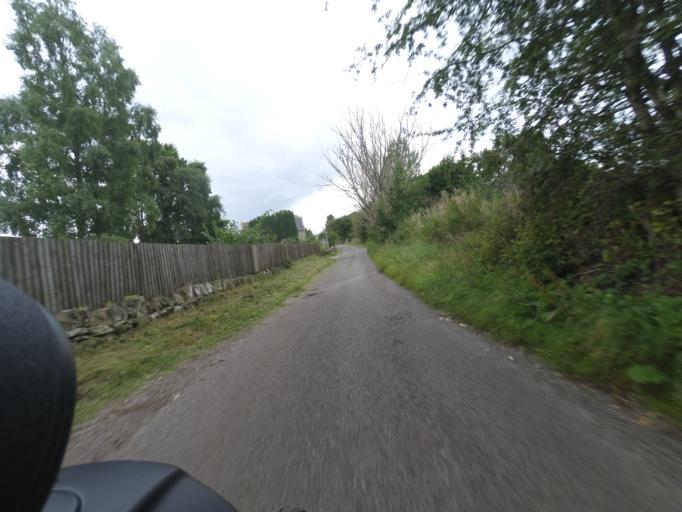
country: GB
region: Scotland
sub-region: Highland
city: Conon Bridge
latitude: 57.5134
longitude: -4.3764
